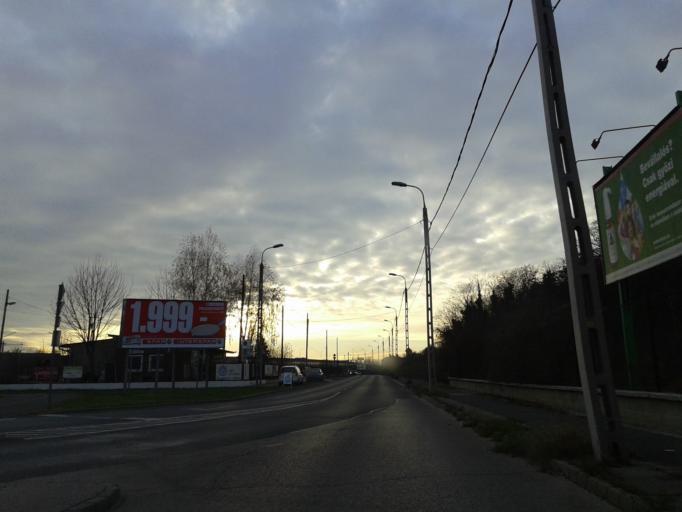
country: HU
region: Budapest
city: Budapest XXII. keruelet
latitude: 47.4028
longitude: 19.0099
